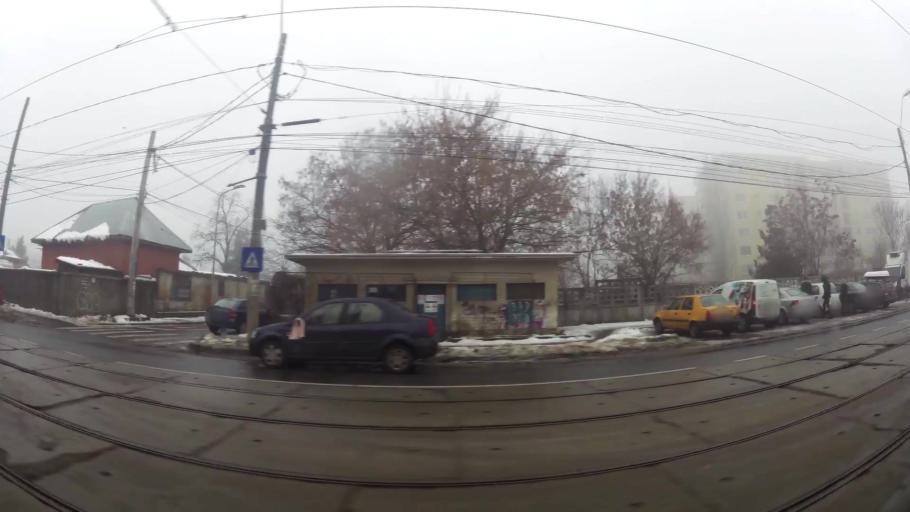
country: RO
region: Ilfov
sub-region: Comuna Chiajna
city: Rosu
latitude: 44.4697
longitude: 26.0246
